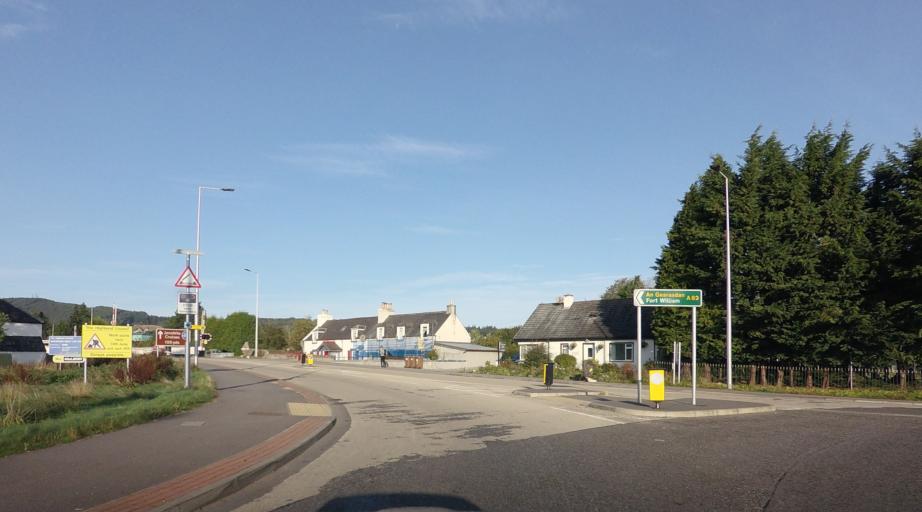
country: GB
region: Scotland
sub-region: Highland
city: Inverness
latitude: 57.4649
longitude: -4.2449
